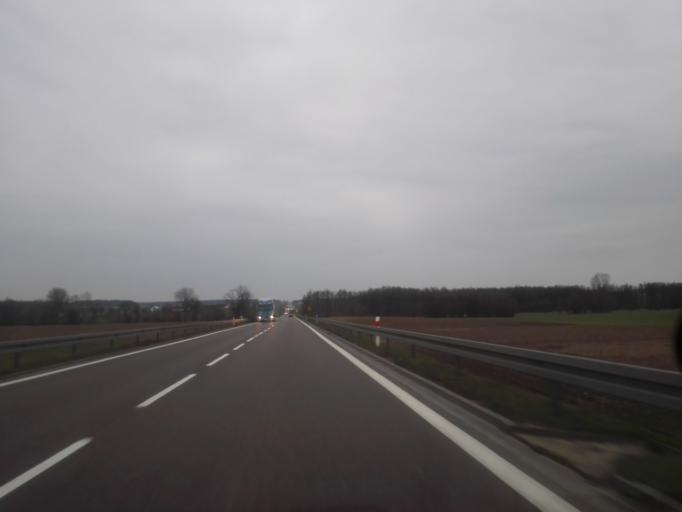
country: PL
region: Podlasie
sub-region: Powiat grajewski
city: Szczuczyn
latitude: 53.5060
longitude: 22.2376
